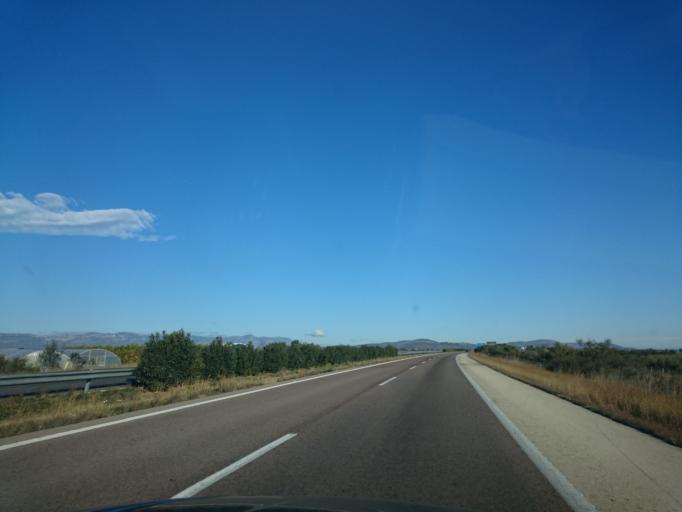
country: ES
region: Catalonia
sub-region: Provincia de Tarragona
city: Ulldecona
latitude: 40.5434
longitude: 0.4192
